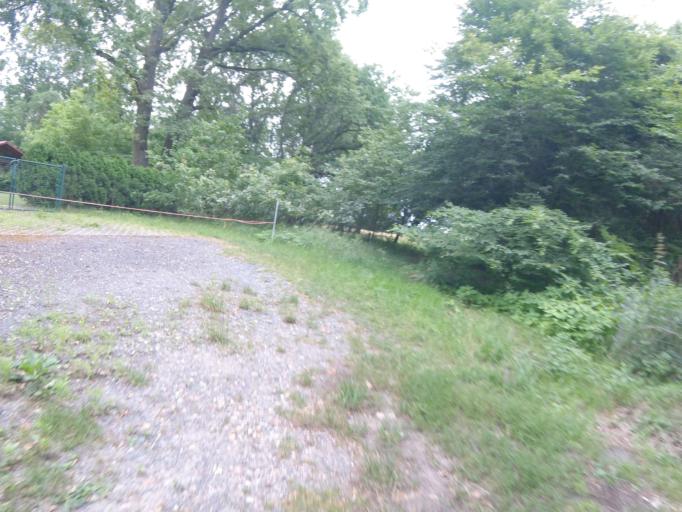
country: DE
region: Brandenburg
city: Mittenwalde
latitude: 52.2358
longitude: 13.5642
